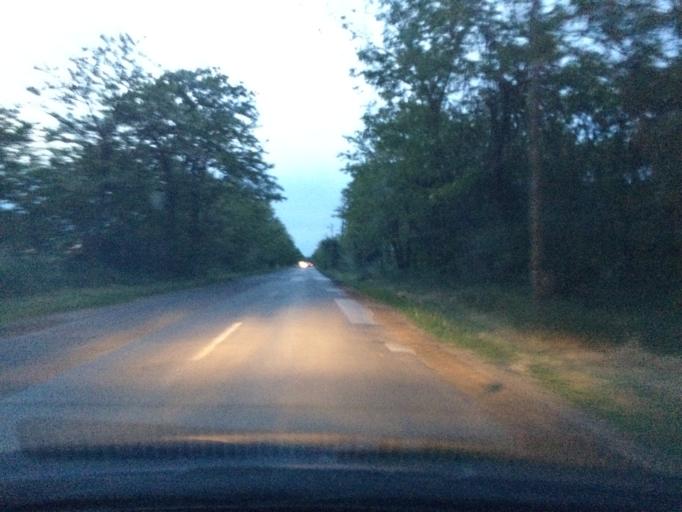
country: HU
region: Hajdu-Bihar
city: Hajdunanas
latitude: 47.9099
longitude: 21.4011
